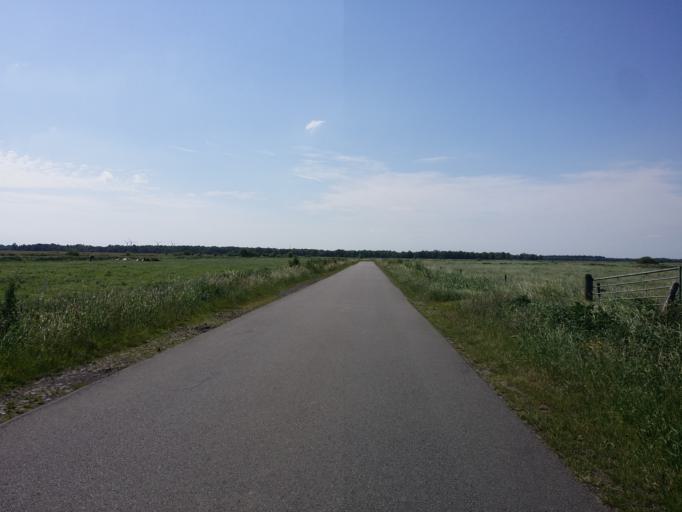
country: DE
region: Lower Saxony
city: Elsfleth
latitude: 53.1974
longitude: 8.3681
